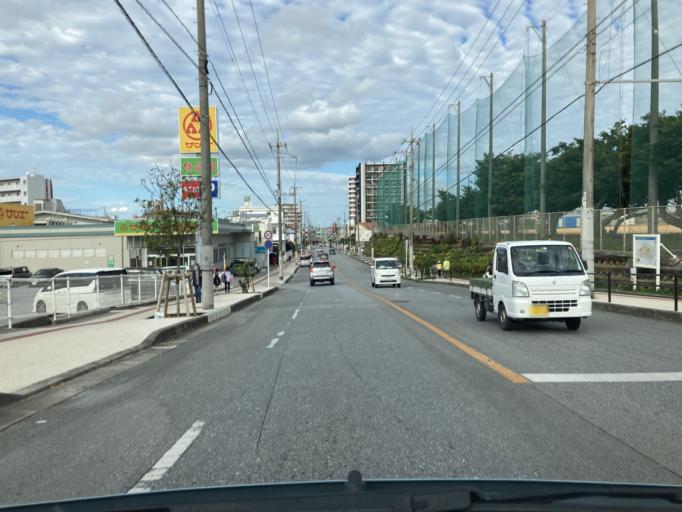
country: JP
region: Okinawa
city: Okinawa
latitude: 26.3384
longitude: 127.8211
